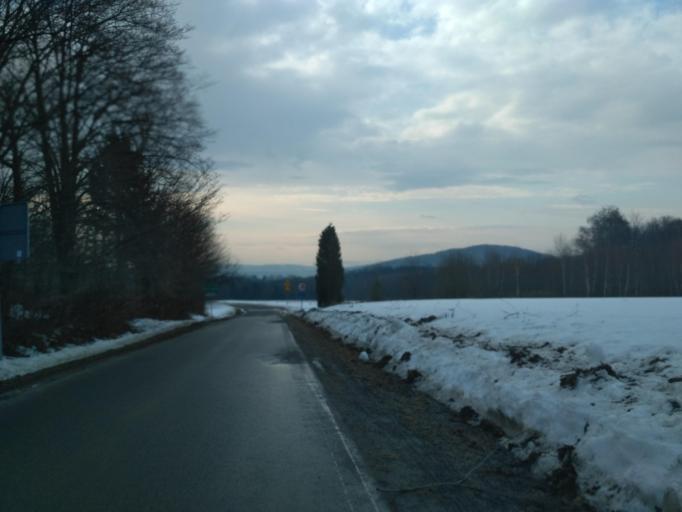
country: PL
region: Subcarpathian Voivodeship
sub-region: Powiat brzozowski
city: Dydnia
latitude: 49.6473
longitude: 22.1601
